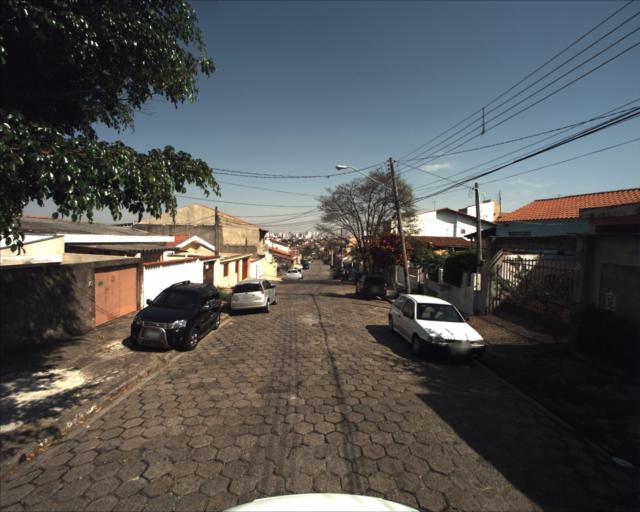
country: BR
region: Sao Paulo
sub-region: Sorocaba
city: Sorocaba
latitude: -23.4806
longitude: -47.4639
